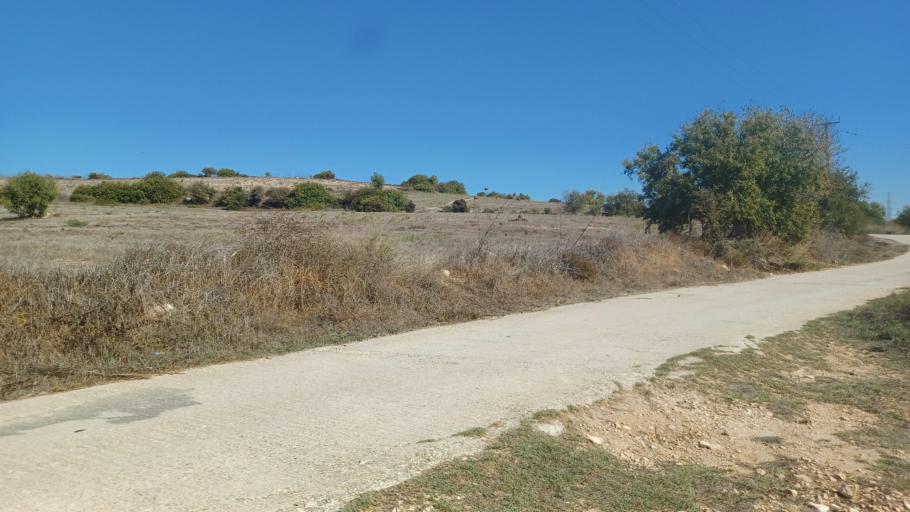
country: CY
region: Pafos
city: Mesogi
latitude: 34.8076
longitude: 32.4903
